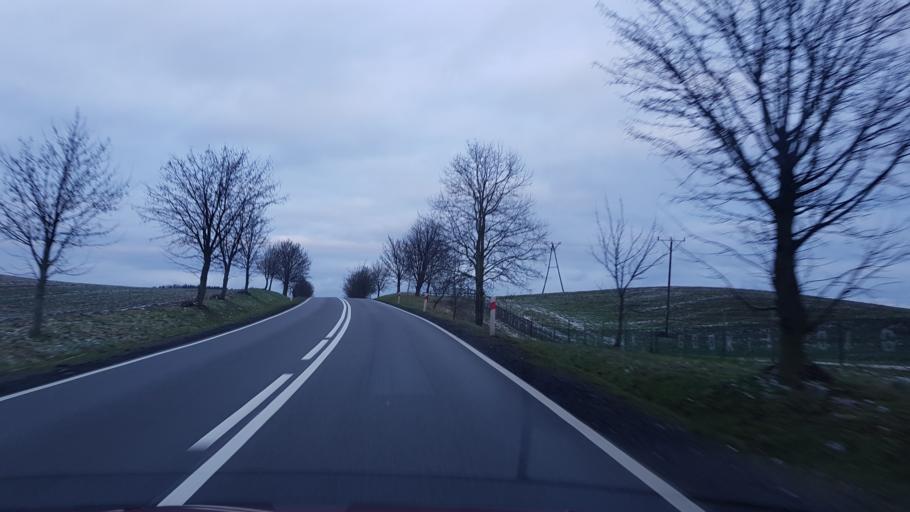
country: PL
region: Pomeranian Voivodeship
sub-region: Powiat bytowski
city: Tuchomie
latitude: 54.0298
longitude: 17.1873
